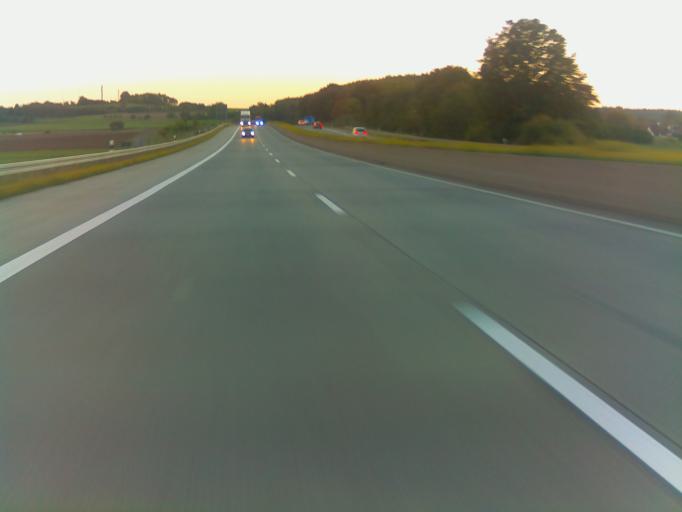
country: DE
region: Hesse
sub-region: Regierungsbezirk Giessen
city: Reiskirchen
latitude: 50.5910
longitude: 8.8115
